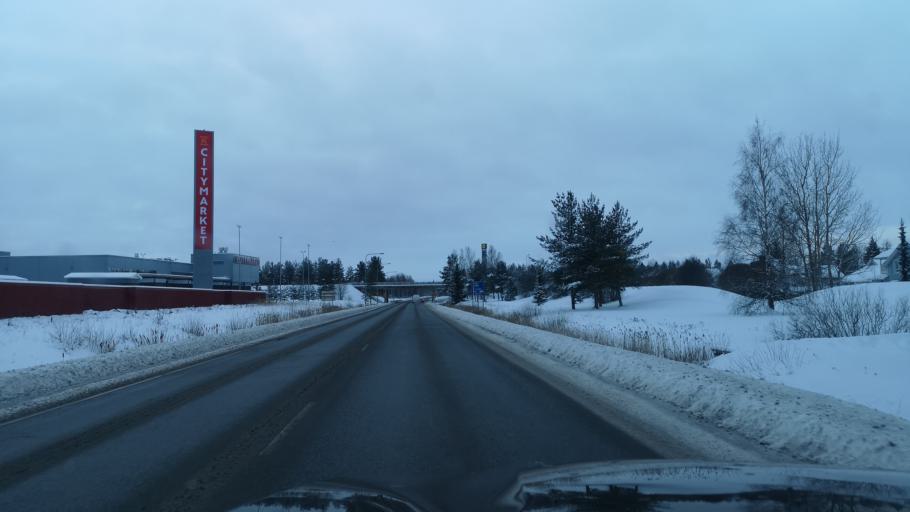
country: FI
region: Varsinais-Suomi
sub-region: Loimaa
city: Loimaa
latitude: 60.8567
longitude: 23.0422
